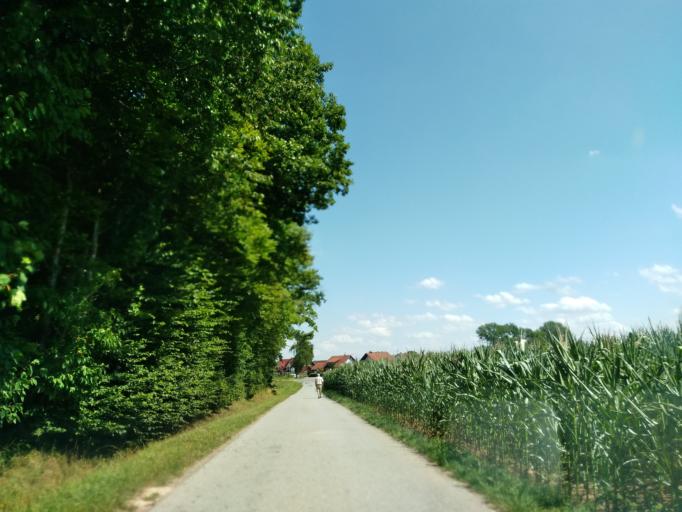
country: DE
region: Baden-Wuerttemberg
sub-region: Karlsruhe Region
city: Limbach
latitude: 49.4720
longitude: 9.2522
